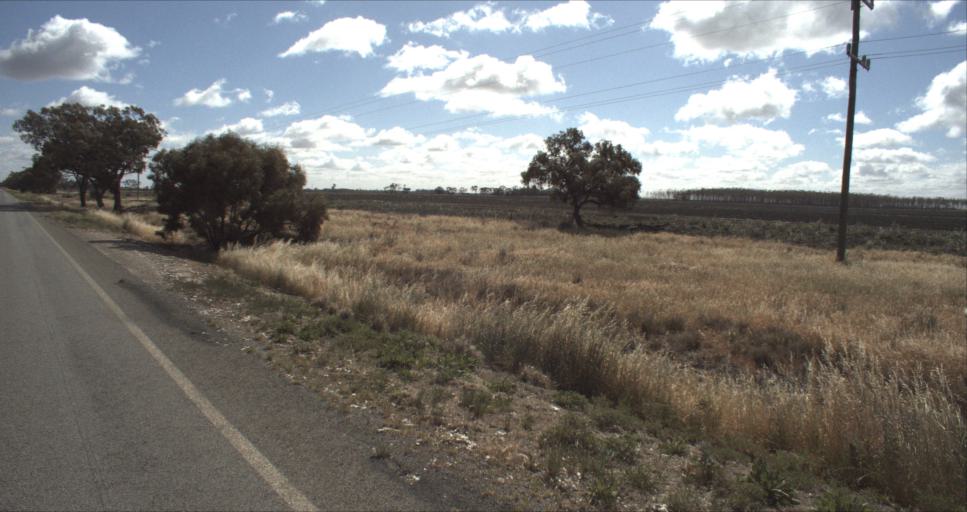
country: AU
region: New South Wales
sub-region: Murrumbidgee Shire
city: Darlington Point
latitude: -34.5629
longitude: 146.1687
